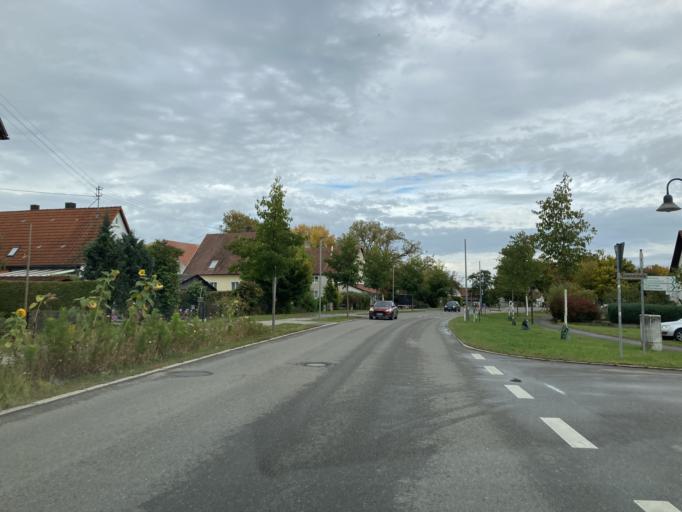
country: DE
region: Baden-Wuerttemberg
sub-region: Regierungsbezirk Stuttgart
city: Bondorf
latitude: 48.5082
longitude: 8.8798
